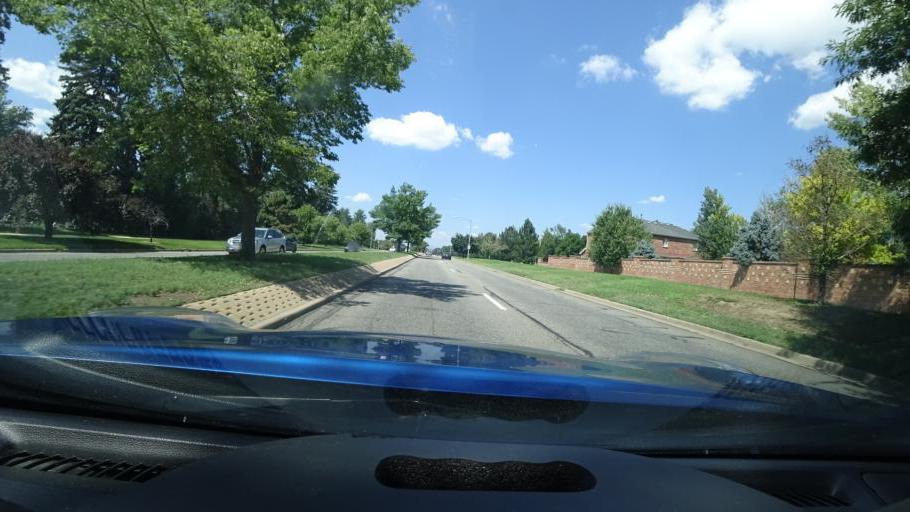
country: US
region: Colorado
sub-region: Arapahoe County
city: Glendale
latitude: 39.7113
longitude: -104.8997
